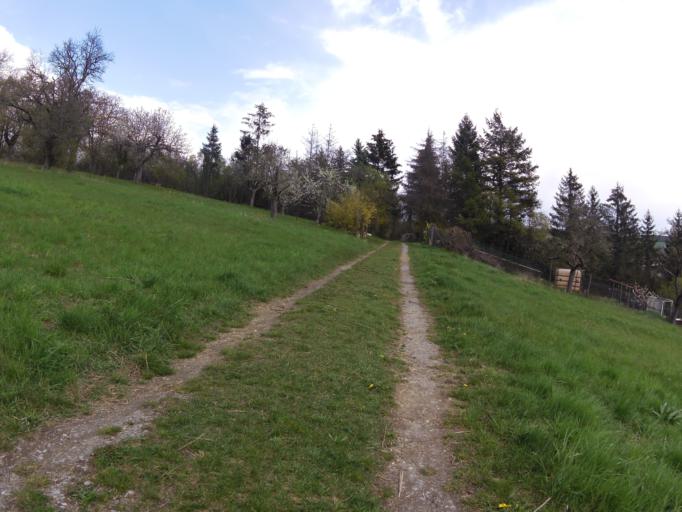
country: DE
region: Bavaria
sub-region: Regierungsbezirk Unterfranken
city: Rimpar
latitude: 49.8598
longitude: 9.9559
